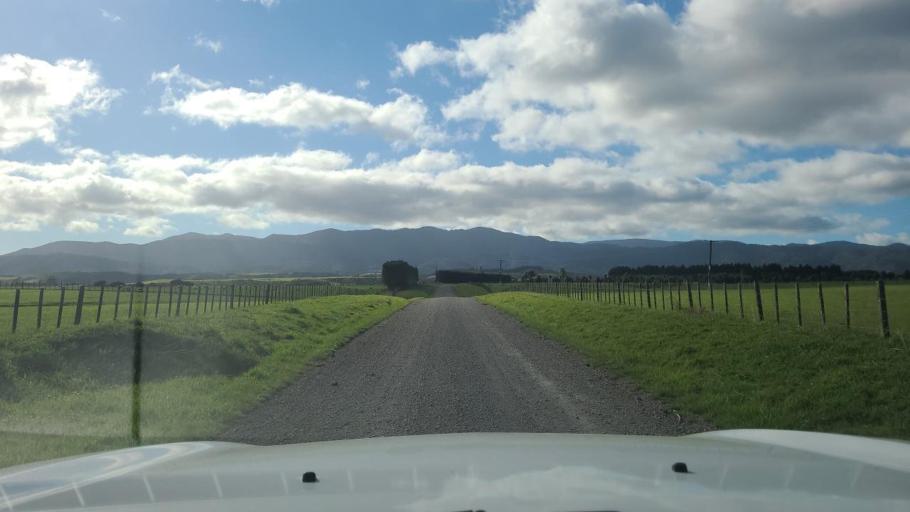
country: NZ
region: Wellington
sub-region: Upper Hutt City
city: Upper Hutt
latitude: -41.3460
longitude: 175.2327
